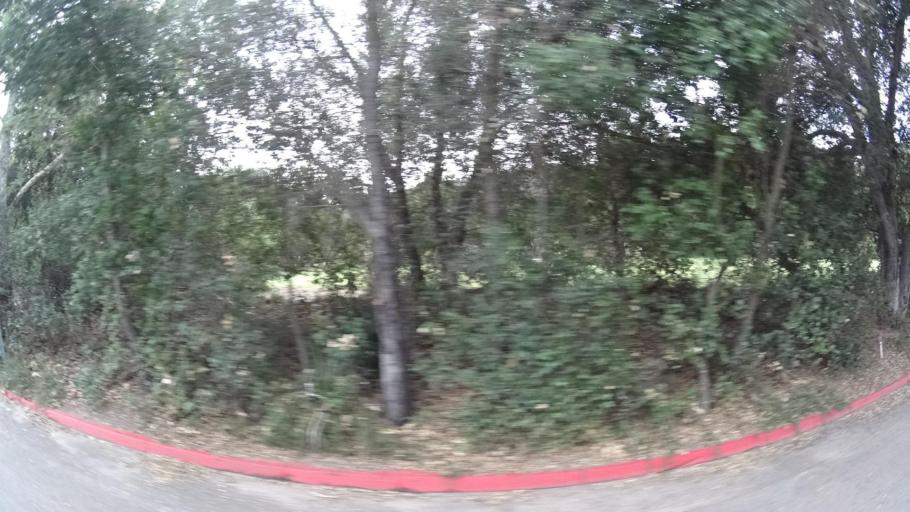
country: US
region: California
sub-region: San Diego County
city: Ramona
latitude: 32.9991
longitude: -116.9411
